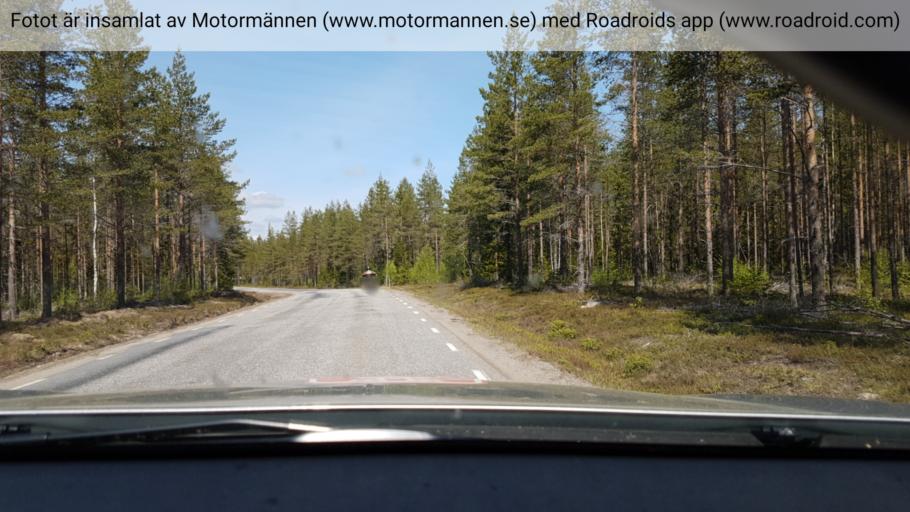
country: SE
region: Vaesterbotten
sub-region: Umea Kommun
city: Saevar
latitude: 63.8781
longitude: 20.5812
